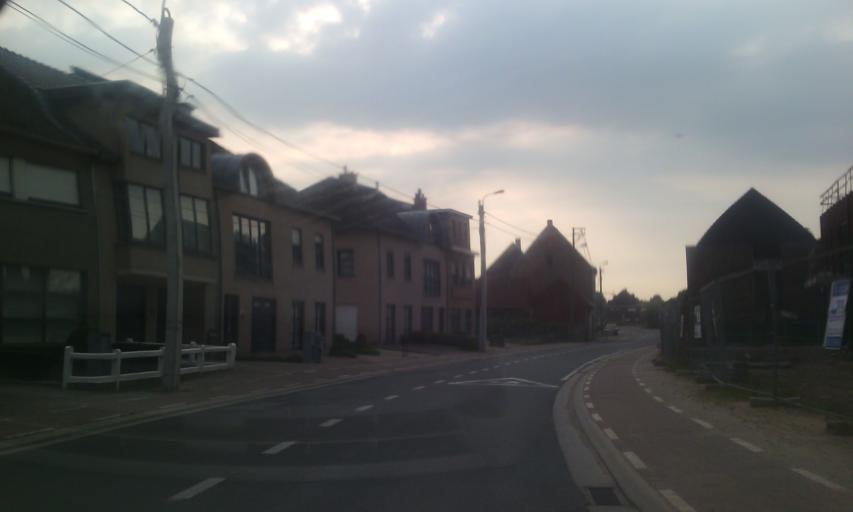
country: BE
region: Flanders
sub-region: Provincie Oost-Vlaanderen
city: Lede
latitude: 50.9637
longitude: 4.0003
